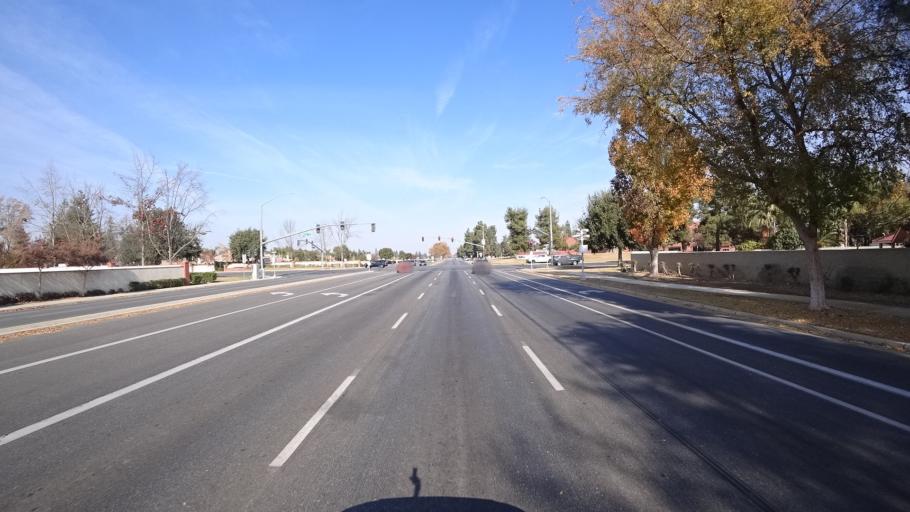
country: US
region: California
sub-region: Kern County
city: Greenacres
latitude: 35.3392
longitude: -119.1142
